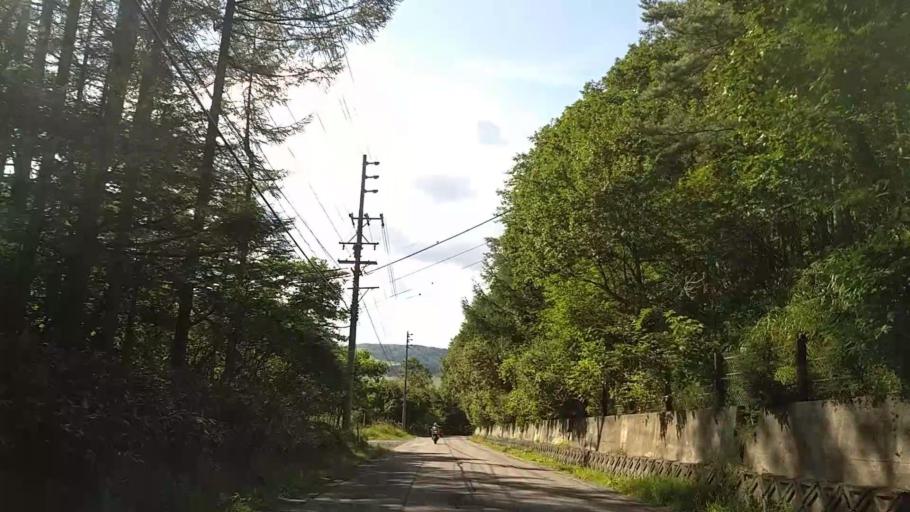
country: JP
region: Nagano
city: Chino
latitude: 36.1009
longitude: 138.2491
